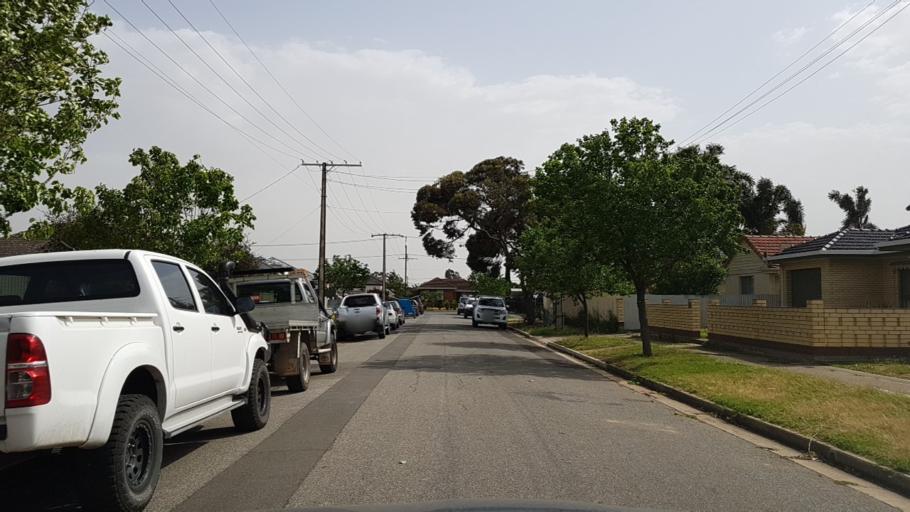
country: AU
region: South Australia
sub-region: Charles Sturt
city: Woodville West
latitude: -34.8887
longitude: 138.5235
